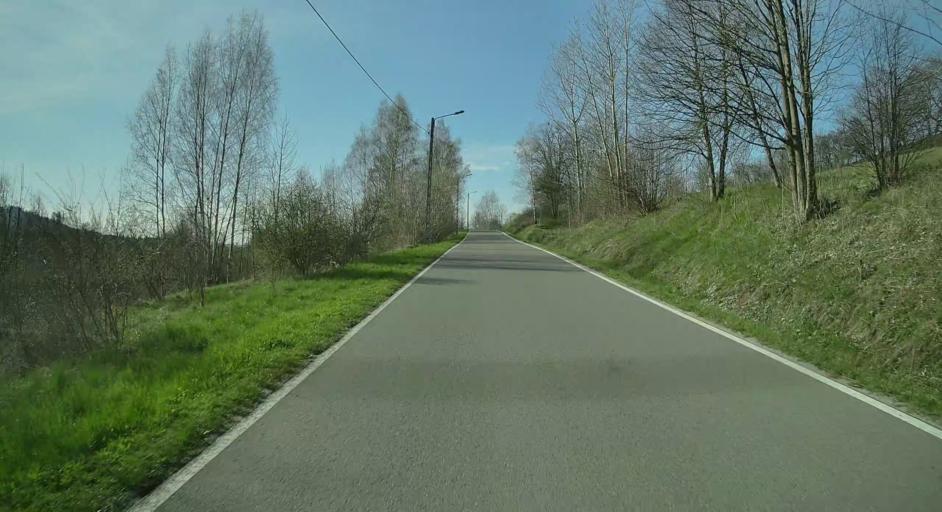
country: PL
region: Lower Silesian Voivodeship
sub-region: Powiat klodzki
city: Lewin Klodzki
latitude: 50.4006
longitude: 16.2947
